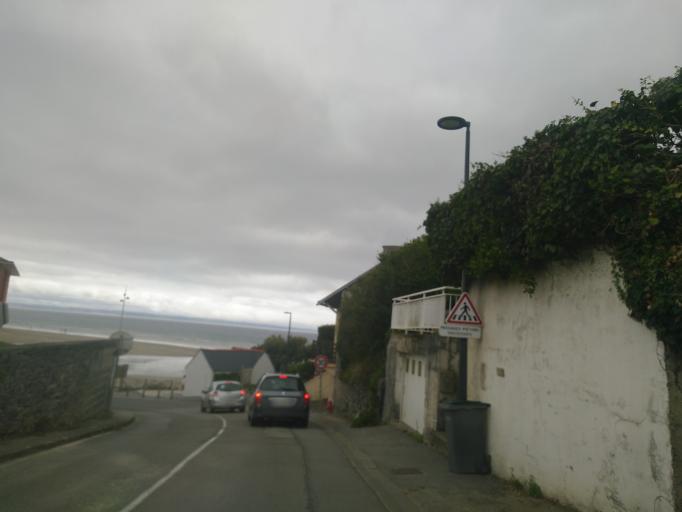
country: FR
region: Brittany
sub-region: Departement du Finistere
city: Telgruc-sur-Mer
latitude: 48.1968
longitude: -4.3034
